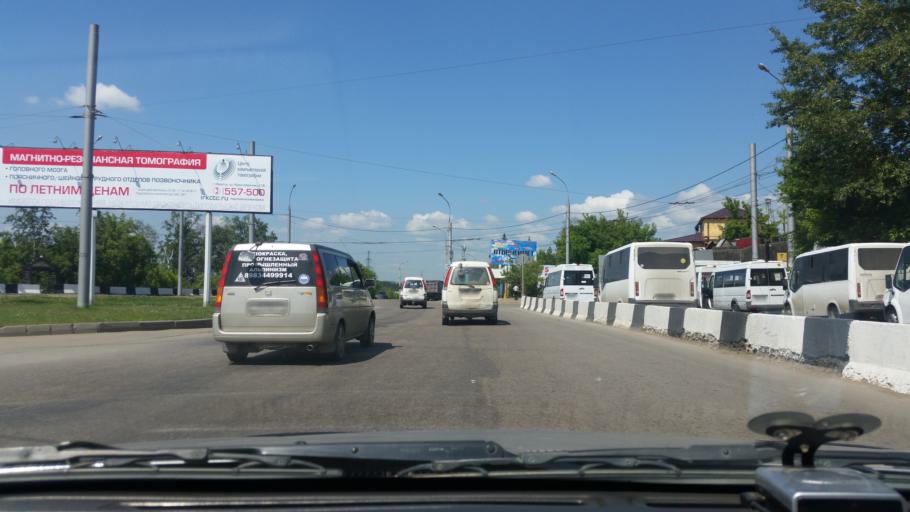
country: RU
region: Irkutsk
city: Smolenshchina
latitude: 52.2597
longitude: 104.1996
